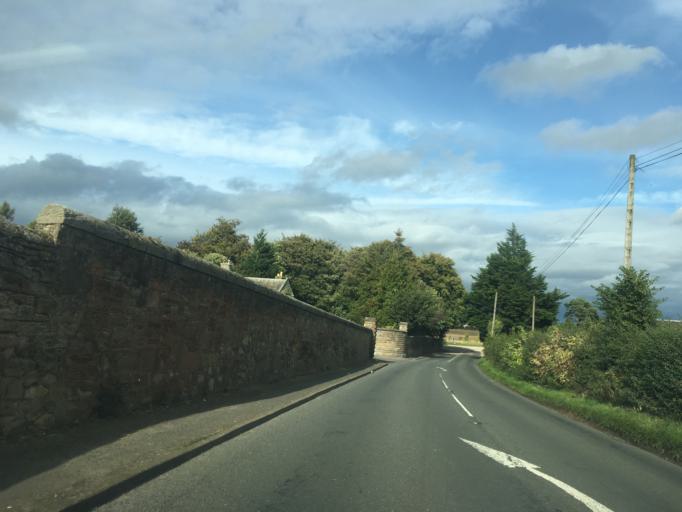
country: GB
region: Scotland
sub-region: East Lothian
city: Musselburgh
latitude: 55.9138
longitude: -3.0438
